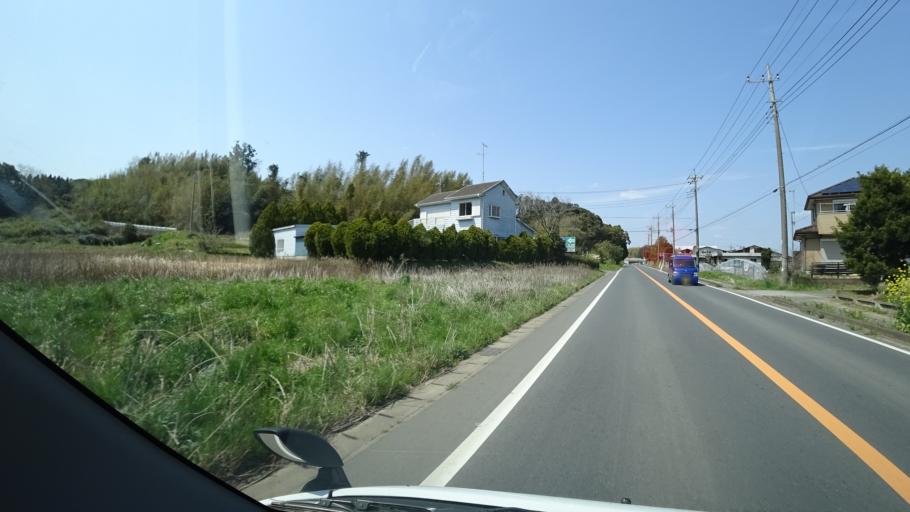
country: JP
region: Chiba
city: Yokaichiba
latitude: 35.7178
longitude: 140.4647
